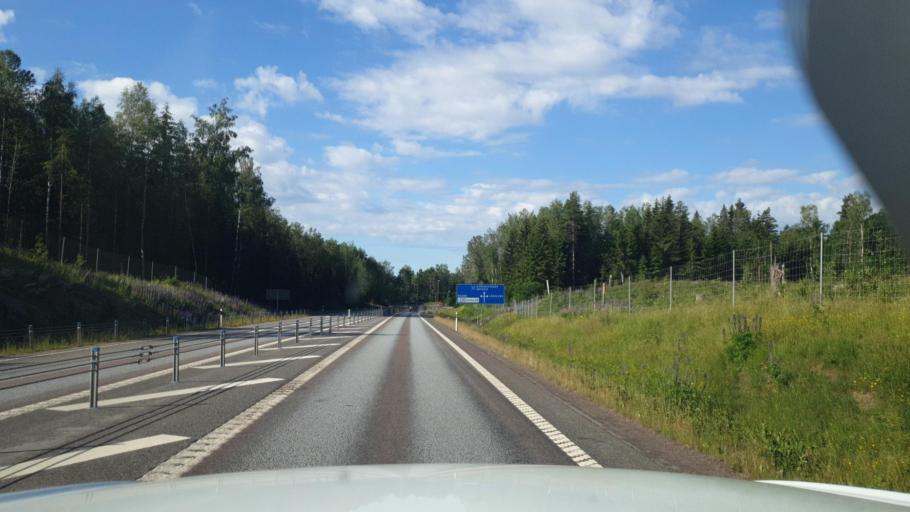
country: SE
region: Vaermland
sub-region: Arvika Kommun
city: Arvika
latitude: 59.6511
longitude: 12.7513
